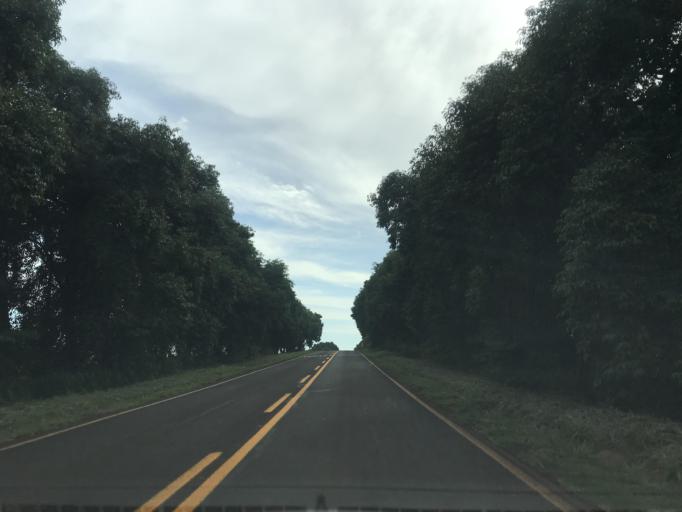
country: BR
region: Parana
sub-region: Terra Rica
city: Terra Rica
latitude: -22.7737
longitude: -52.6505
